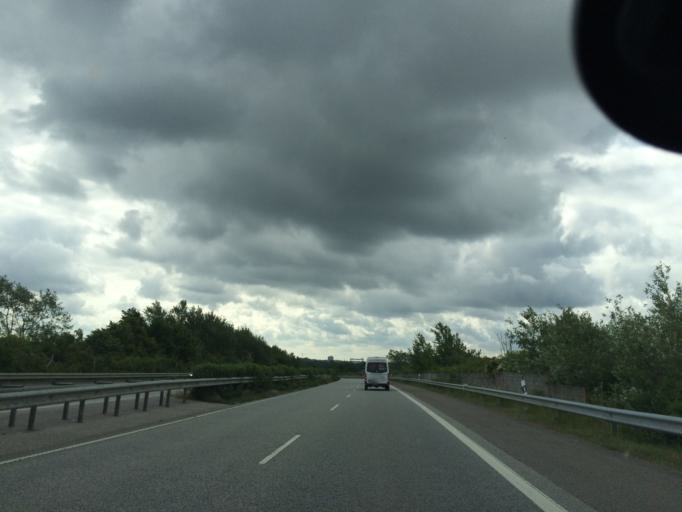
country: DE
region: Schleswig-Holstein
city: Kronshagen
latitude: 54.3664
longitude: 10.0801
